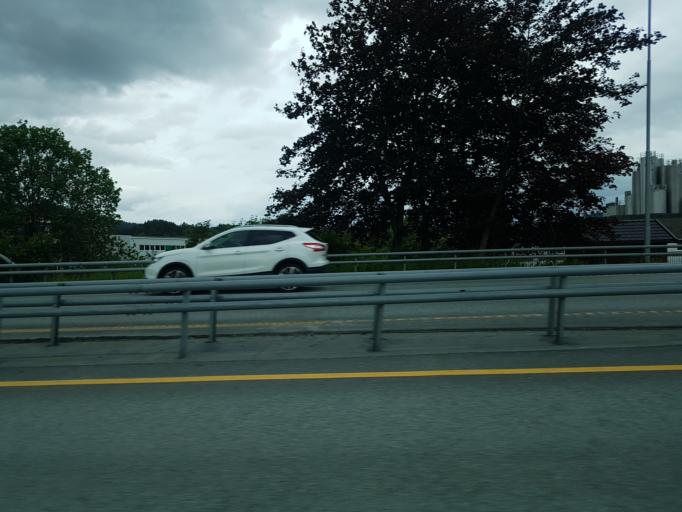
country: NO
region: Nord-Trondelag
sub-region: Stjordal
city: Stjordal
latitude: 63.4773
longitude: 10.9018
